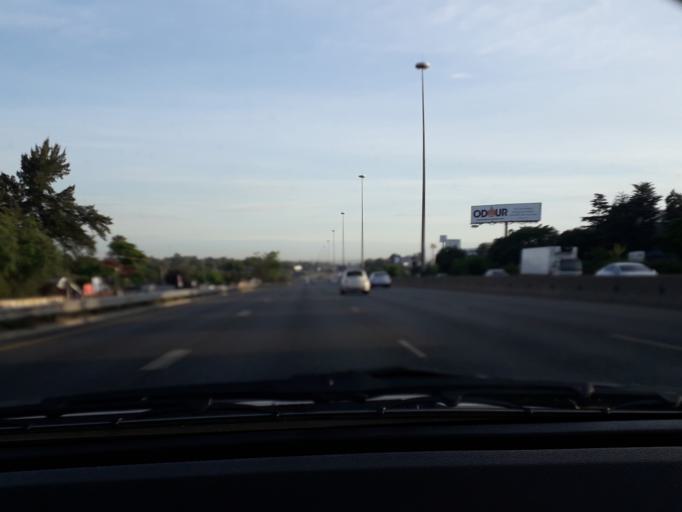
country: ZA
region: Gauteng
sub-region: City of Johannesburg Metropolitan Municipality
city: Modderfontein
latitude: -26.0828
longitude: 28.0867
